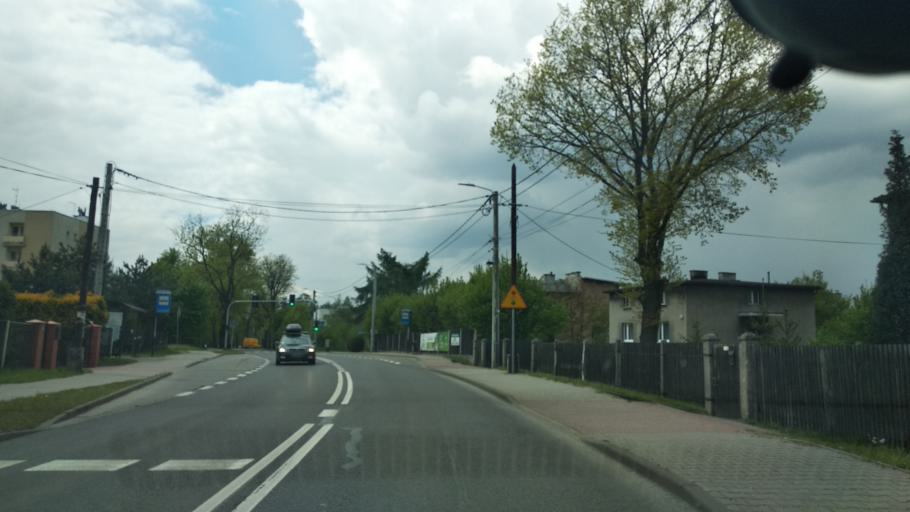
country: PL
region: Silesian Voivodeship
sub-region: Powiat mikolowski
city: Mikolow
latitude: 50.2296
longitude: 18.9375
